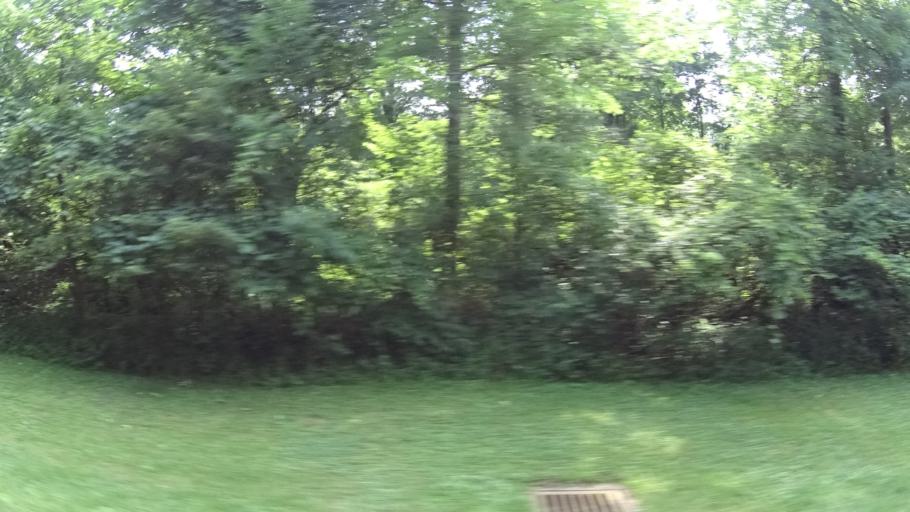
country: US
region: Ohio
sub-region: Lorain County
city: Vermilion
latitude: 41.3720
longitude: -82.4054
